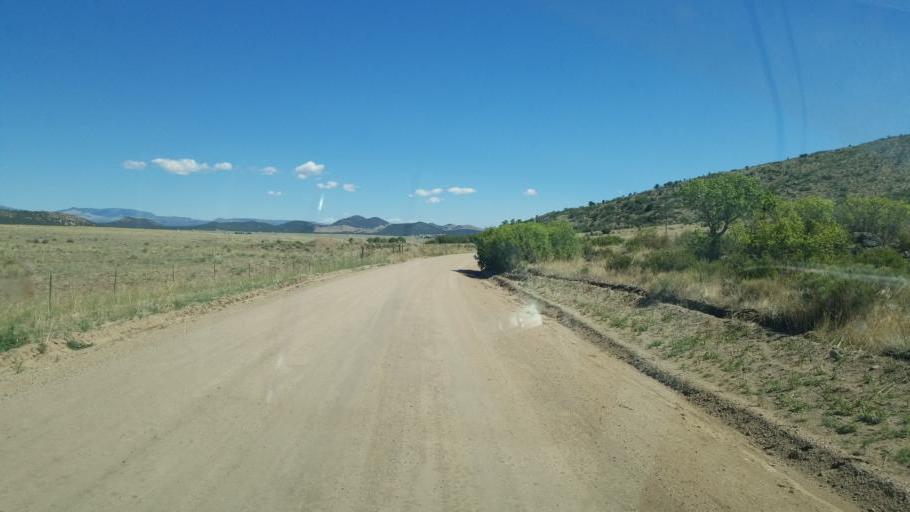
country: US
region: Colorado
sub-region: Custer County
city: Westcliffe
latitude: 38.2391
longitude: -105.5020
